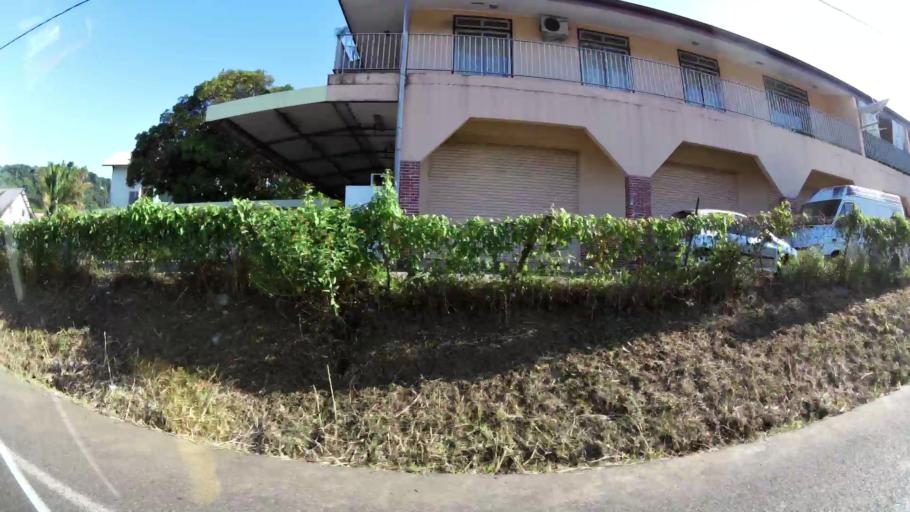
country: GF
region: Guyane
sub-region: Guyane
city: Remire-Montjoly
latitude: 4.8874
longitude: -52.2777
